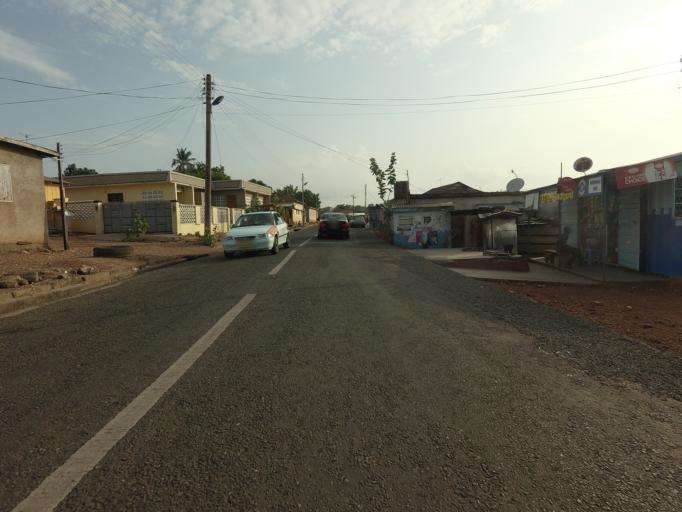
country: GH
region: Volta
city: Ho
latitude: 6.6071
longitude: 0.4713
